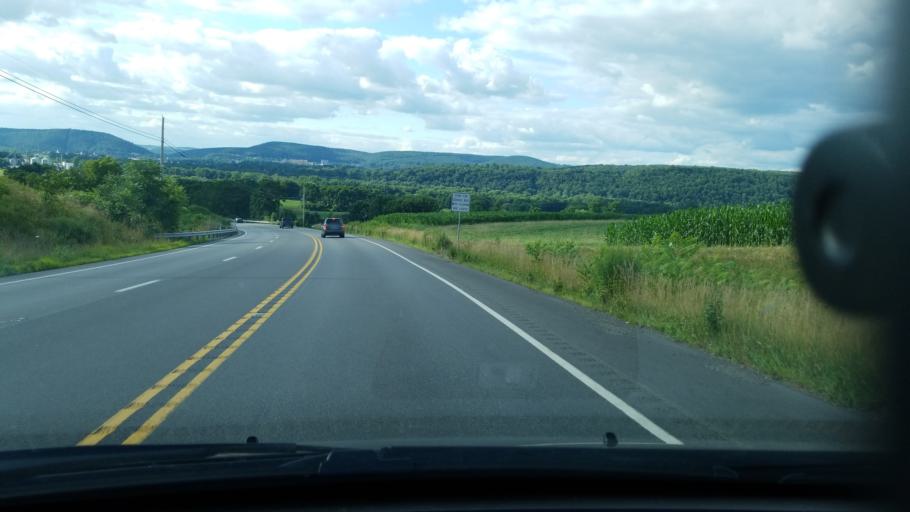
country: US
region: Pennsylvania
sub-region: Montour County
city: Mechanicsville
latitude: 40.9265
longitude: -76.5883
